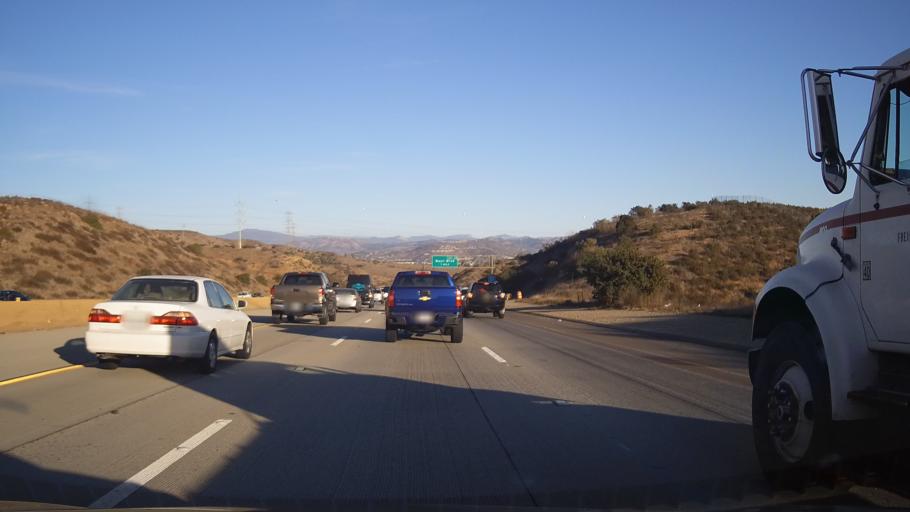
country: US
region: California
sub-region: San Diego County
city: Santee
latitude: 32.8526
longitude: -117.0475
